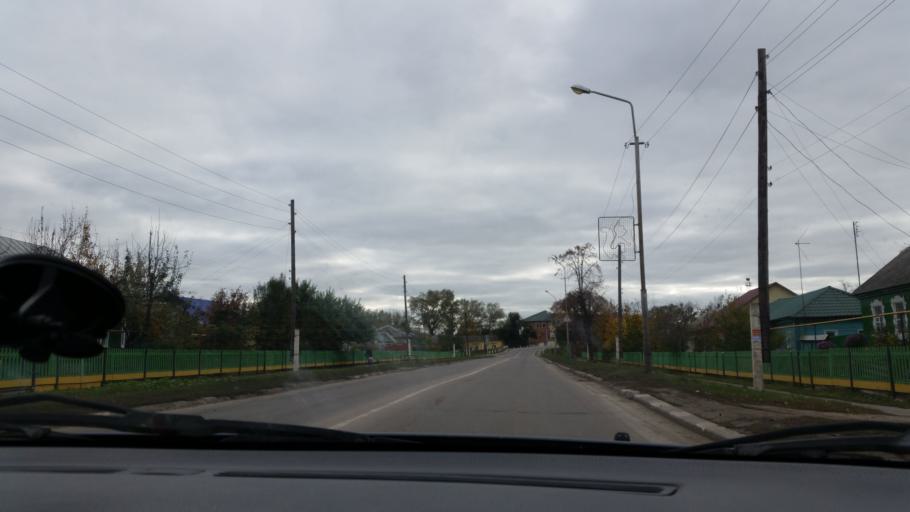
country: RU
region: Lipetsk
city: Gryazi
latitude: 52.4892
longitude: 39.9494
